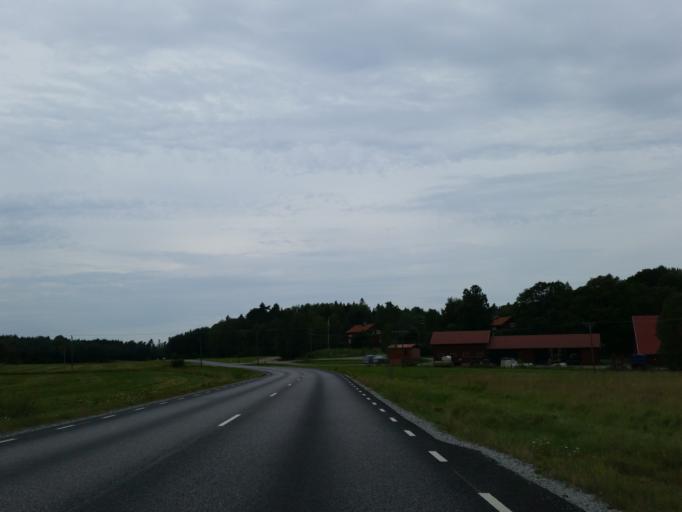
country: SE
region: Stockholm
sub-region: Salems Kommun
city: Ronninge
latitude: 59.2200
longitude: 17.7543
